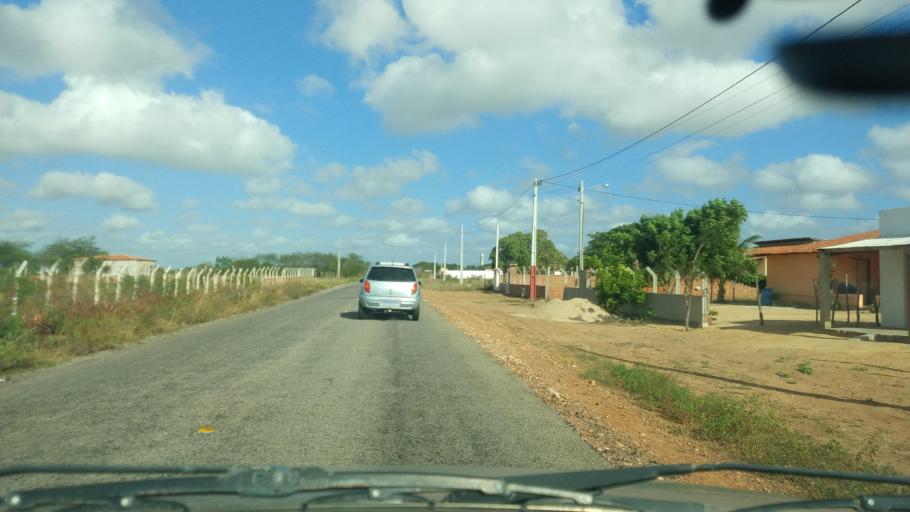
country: BR
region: Rio Grande do Norte
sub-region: Sao Paulo Do Potengi
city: Sao Paulo do Potengi
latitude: -5.9162
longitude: -35.7198
